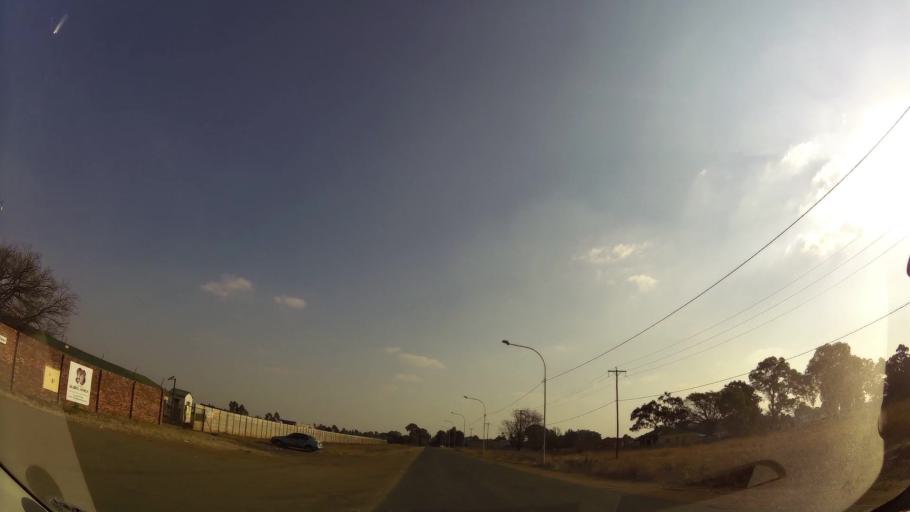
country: ZA
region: Gauteng
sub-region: Ekurhuleni Metropolitan Municipality
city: Benoni
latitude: -26.1043
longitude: 28.3796
